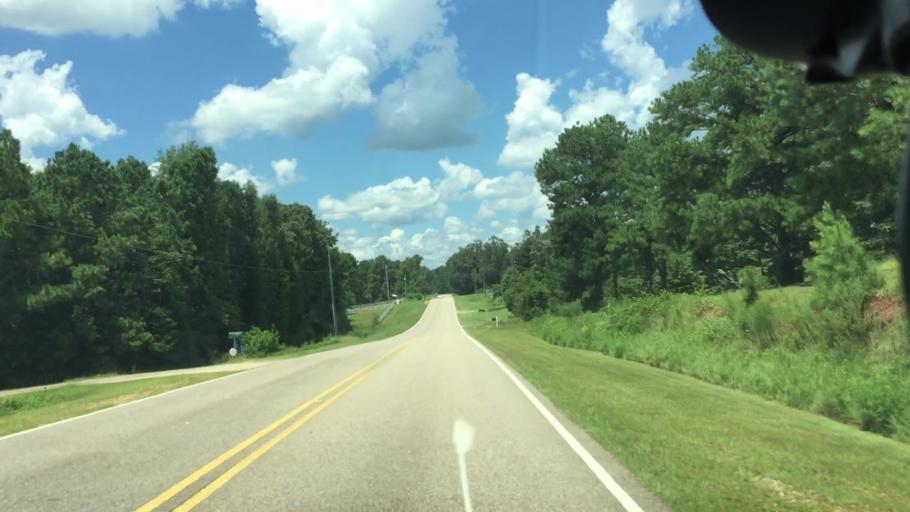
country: US
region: Alabama
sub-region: Coffee County
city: Enterprise
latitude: 31.4022
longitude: -85.8382
